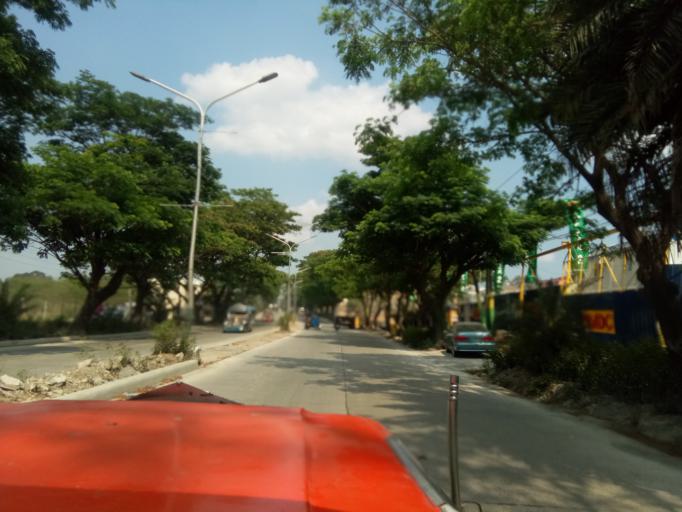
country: PH
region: Calabarzon
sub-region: Province of Cavite
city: Dasmarinas
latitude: 14.3266
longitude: 120.9463
